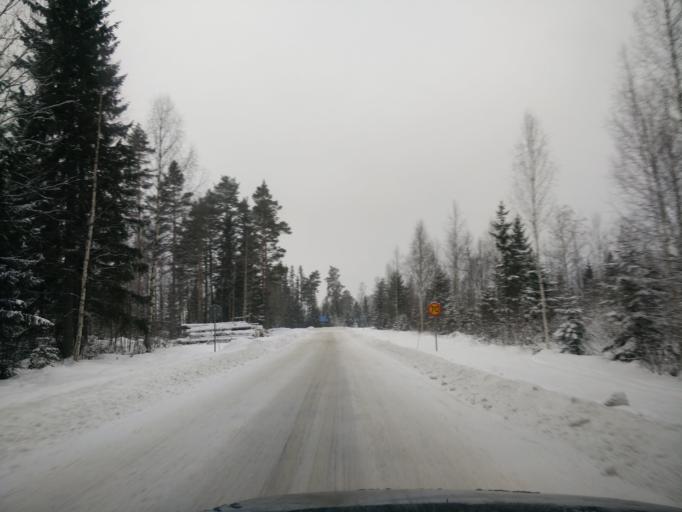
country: SE
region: Vaesternorrland
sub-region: Ange Kommun
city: Ange
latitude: 62.4641
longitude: 15.4410
